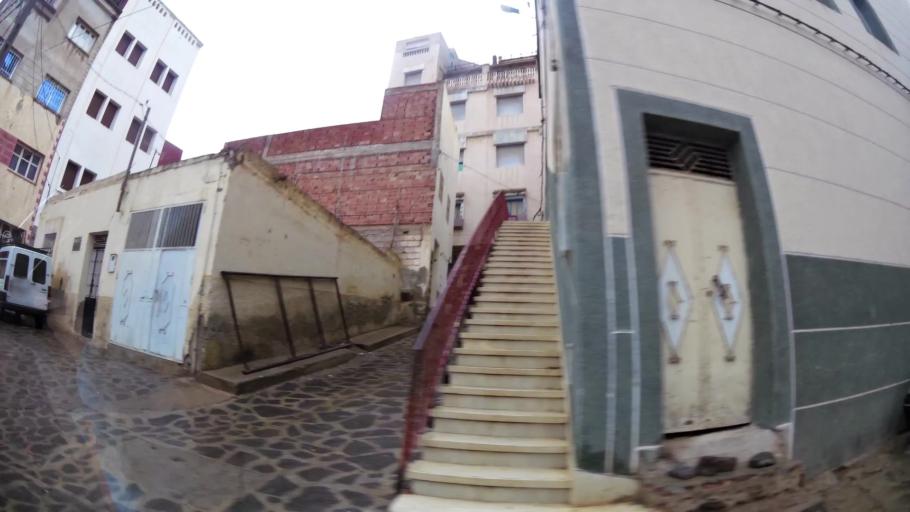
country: MA
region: Oriental
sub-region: Nador
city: Nador
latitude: 35.1756
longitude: -2.9375
